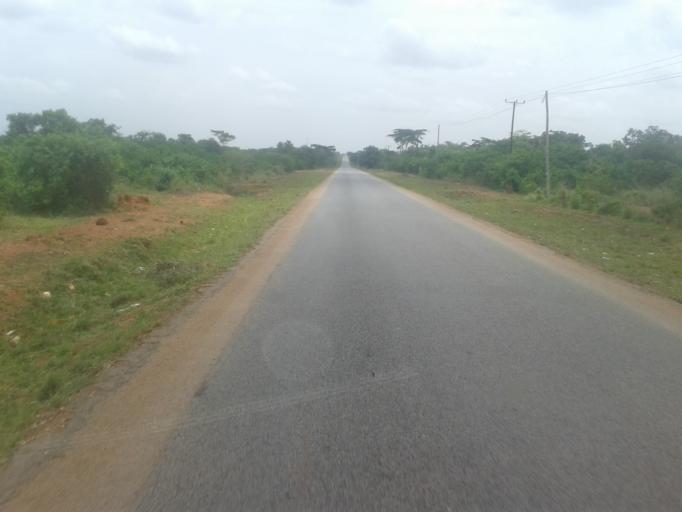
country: UG
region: Western Region
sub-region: Kiryandongo District
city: Masindi Port
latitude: 1.4758
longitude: 32.1430
